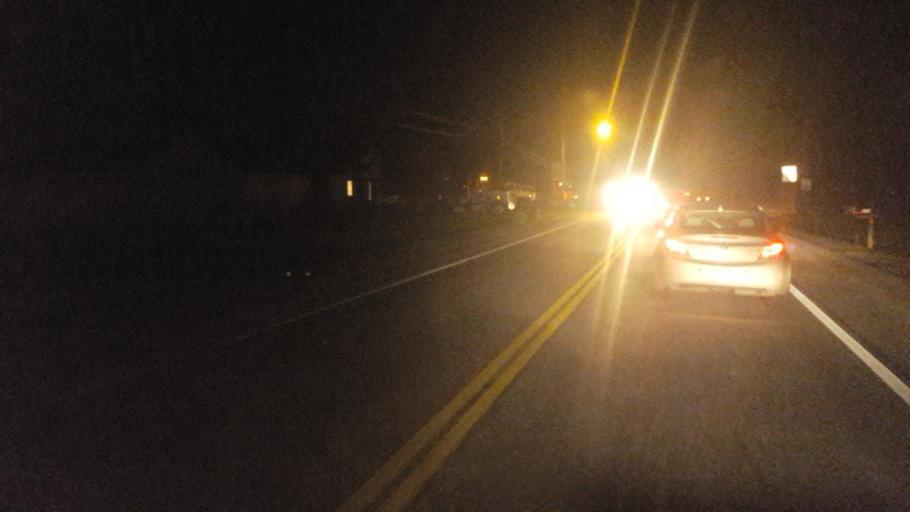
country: US
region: Ohio
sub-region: Wayne County
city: Apple Creek
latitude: 40.7431
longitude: -81.8285
